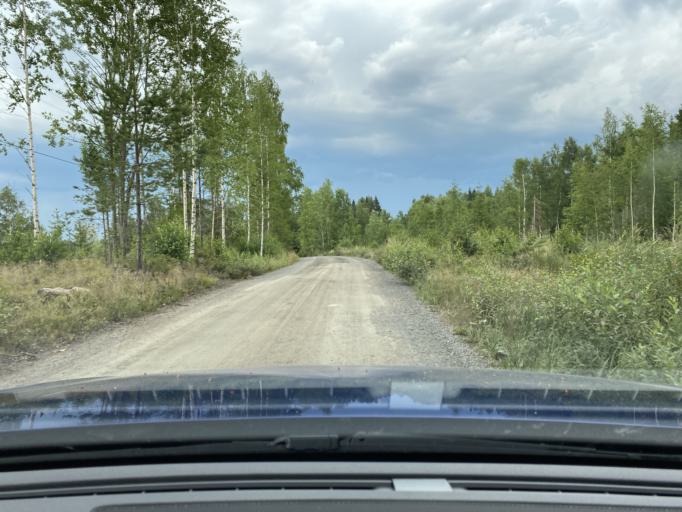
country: FI
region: Satakunta
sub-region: Rauma
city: Lappi
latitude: 61.1360
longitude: 21.9028
